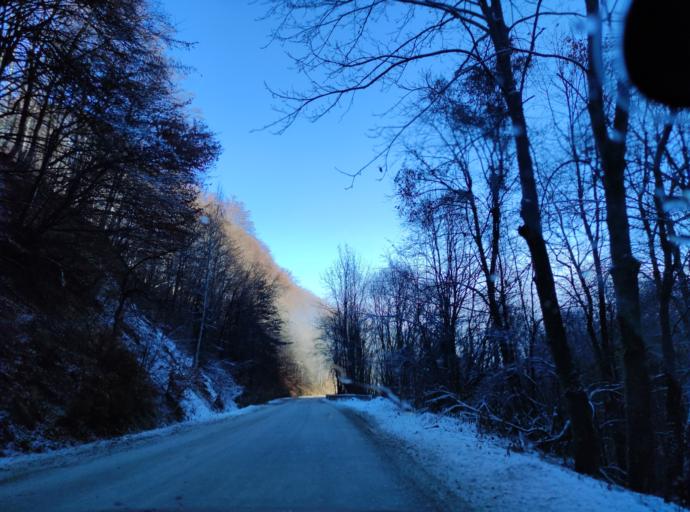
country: BG
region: Sofia-Capital
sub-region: Stolichna Obshtina
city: Sofia
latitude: 42.6086
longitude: 23.2955
